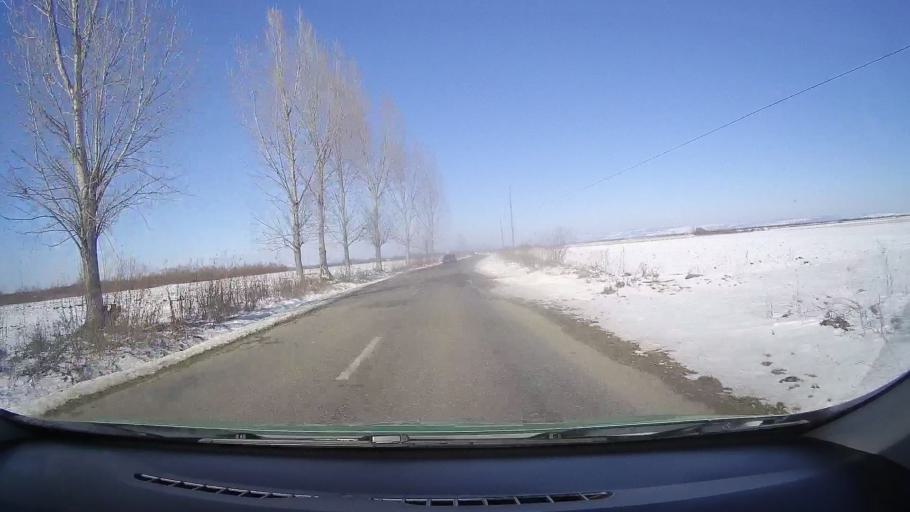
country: RO
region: Brasov
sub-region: Comuna Harseni
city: Harseni
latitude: 45.7397
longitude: 25.0207
